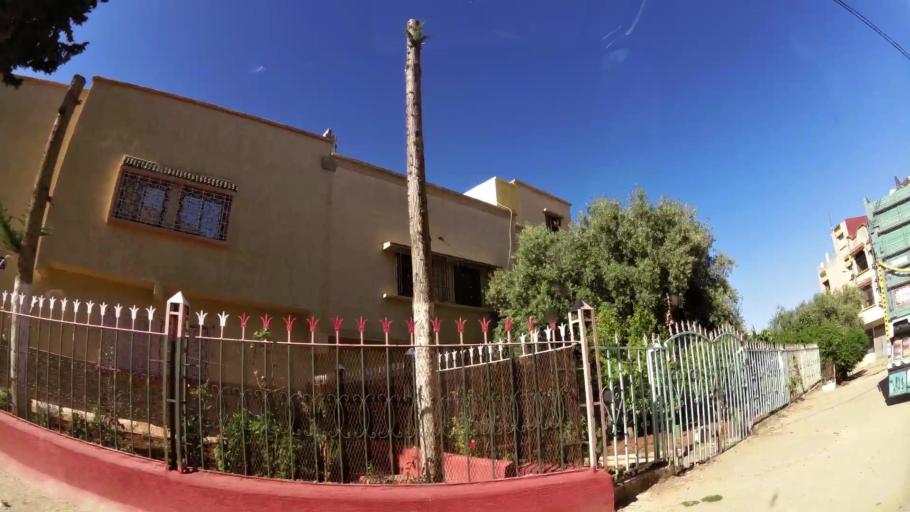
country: MA
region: Meknes-Tafilalet
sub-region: Meknes
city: Meknes
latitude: 33.8968
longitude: -5.5004
